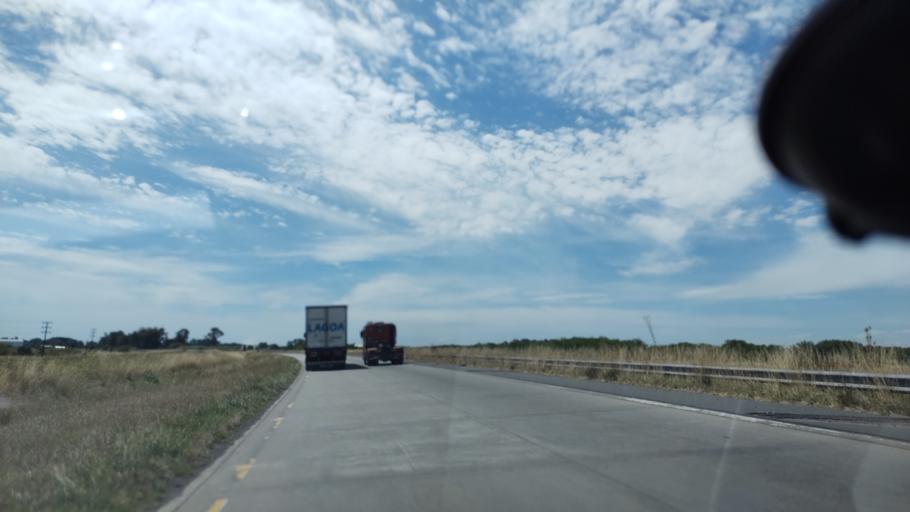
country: AR
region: Buenos Aires
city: Canuelas
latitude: -35.0455
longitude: -58.7109
